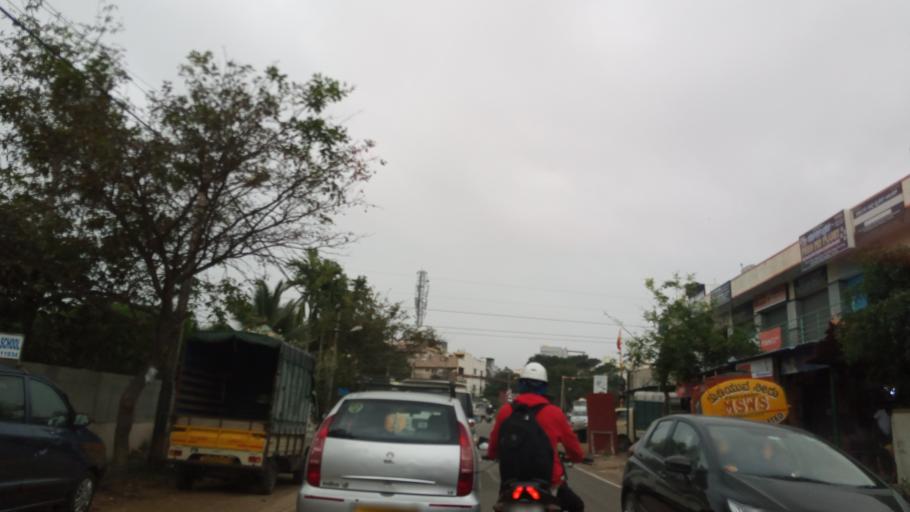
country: IN
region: Karnataka
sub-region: Bangalore Urban
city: Bangalore
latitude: 12.9084
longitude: 77.5371
